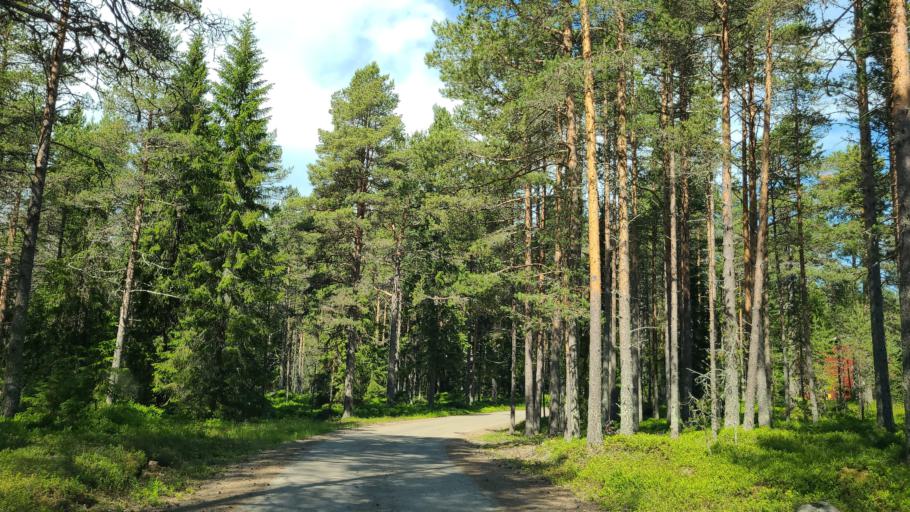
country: SE
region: Vaesterbotten
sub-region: Robertsfors Kommun
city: Robertsfors
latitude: 64.1401
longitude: 20.9616
